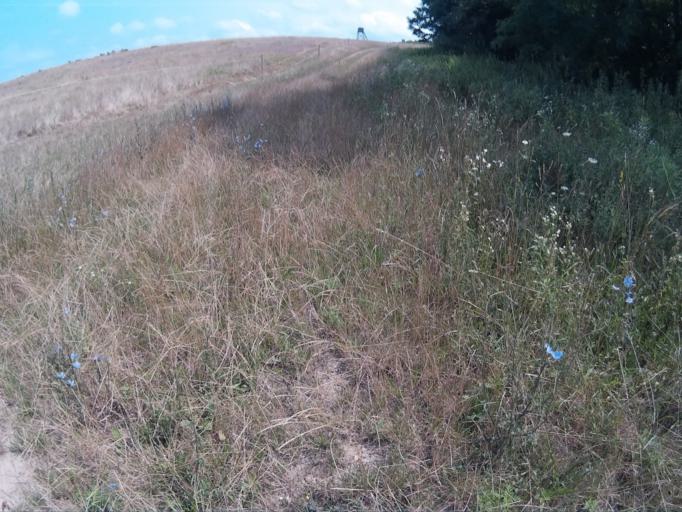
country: HU
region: Veszprem
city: Papa
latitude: 47.2904
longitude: 17.6120
